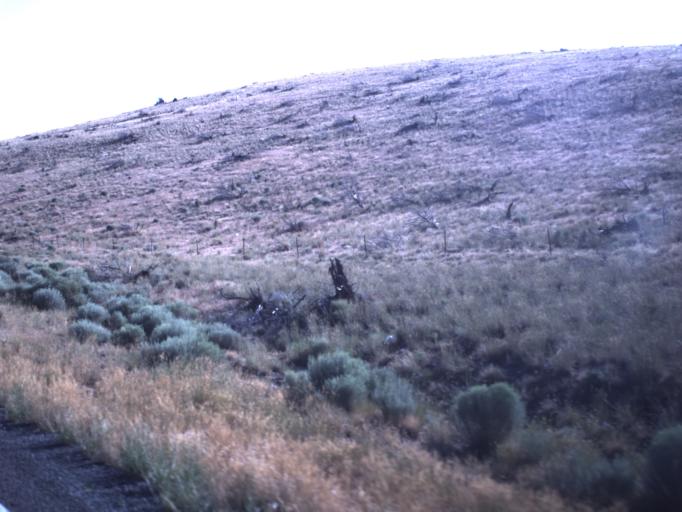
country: US
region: Utah
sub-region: Iron County
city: Parowan
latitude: 38.0773
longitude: -112.9577
